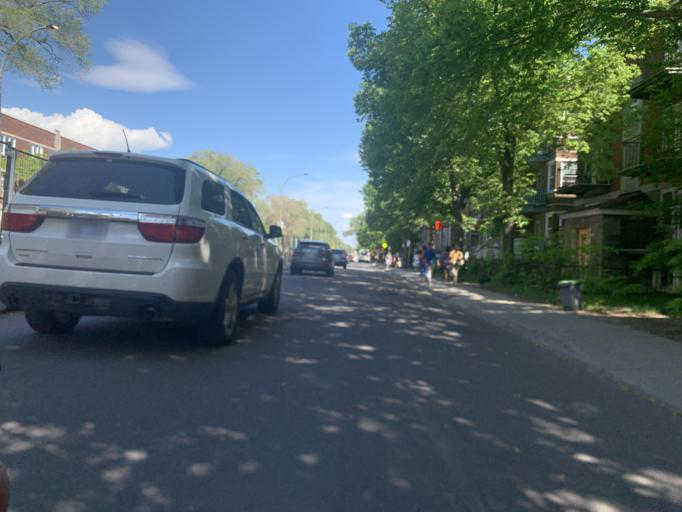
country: CA
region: Quebec
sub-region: Monteregie
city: Longueuil
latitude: 45.5533
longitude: -73.5509
